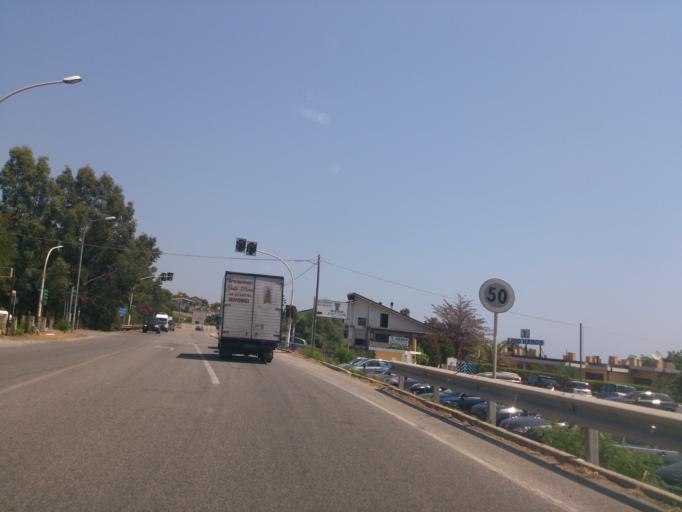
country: IT
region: Calabria
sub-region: Provincia di Reggio Calabria
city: Riace Marina
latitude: 38.3867
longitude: 16.5264
